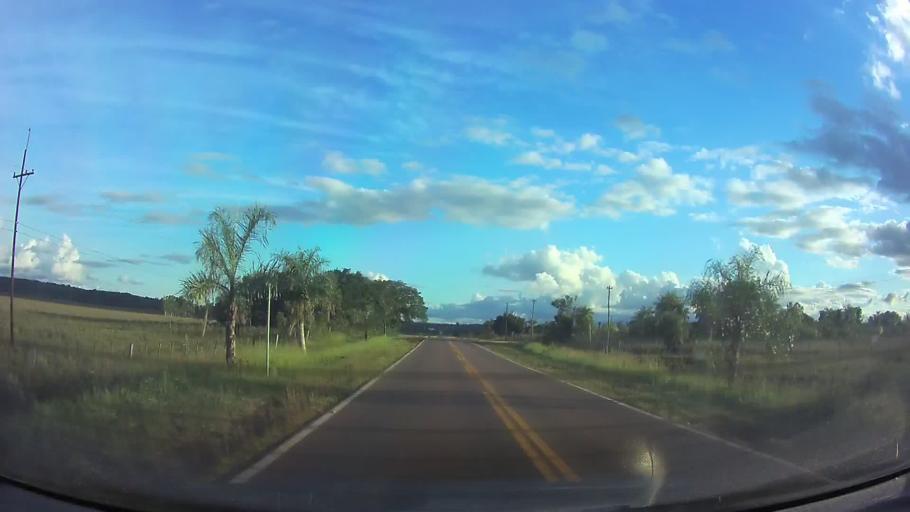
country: PY
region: Paraguari
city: Acahay
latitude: -25.8779
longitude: -57.1234
